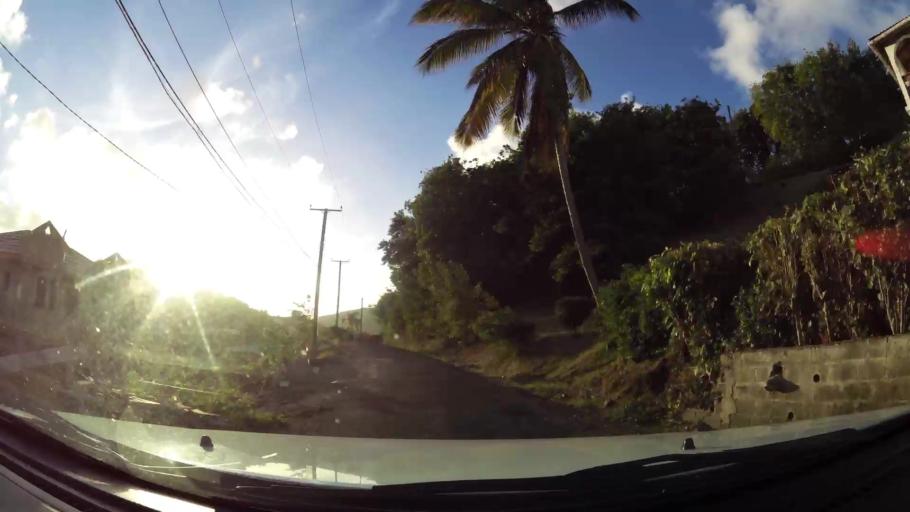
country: LC
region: Gros-Islet
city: Gros Islet
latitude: 14.0683
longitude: -60.9418
